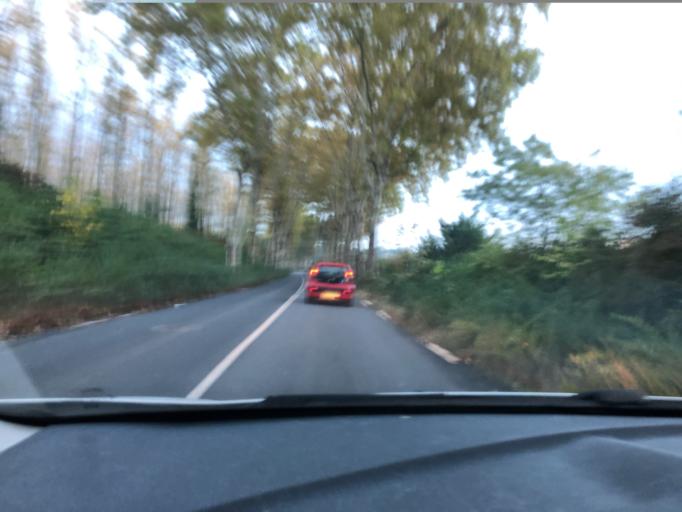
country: FR
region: Languedoc-Roussillon
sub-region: Departement de l'Herault
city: Montferrier-sur-Lez
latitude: 43.6594
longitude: 3.8632
